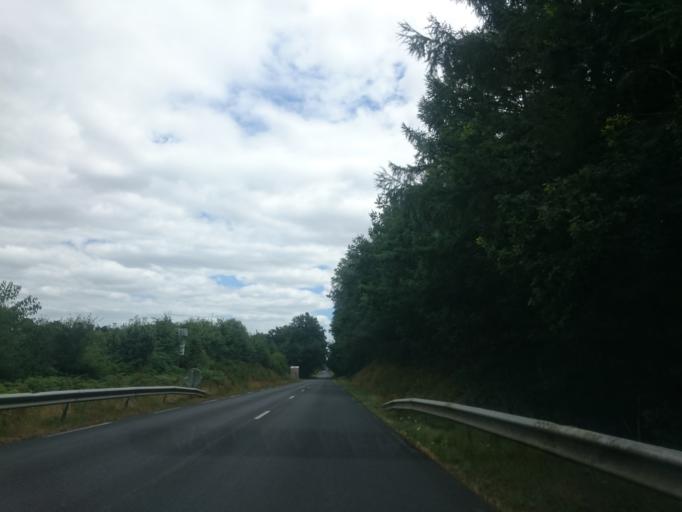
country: FR
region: Auvergne
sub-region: Departement du Cantal
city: Laroquebrou
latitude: 44.9677
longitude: 2.2408
